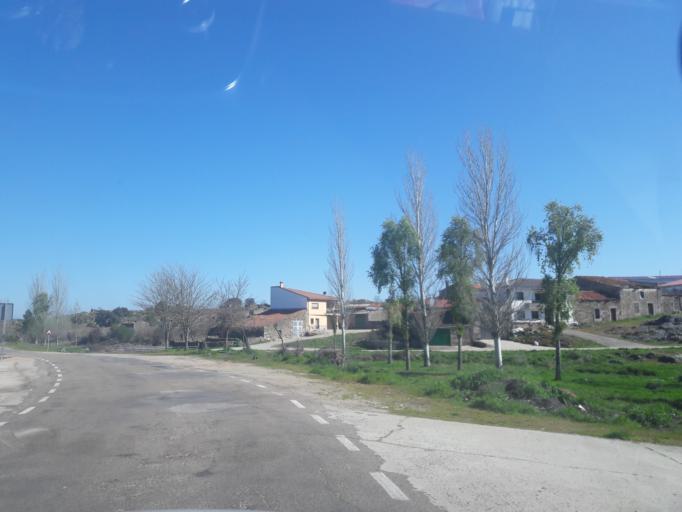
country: ES
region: Castille and Leon
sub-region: Provincia de Salamanca
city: Valsalabroso
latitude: 41.1548
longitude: -6.4879
